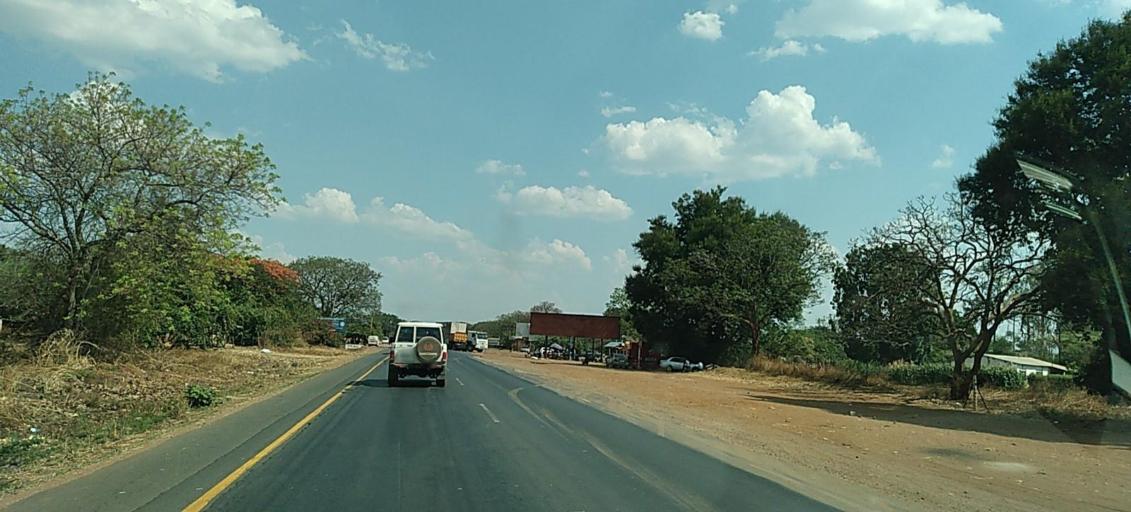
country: ZM
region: Central
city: Chibombo
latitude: -14.8793
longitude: 28.0604
